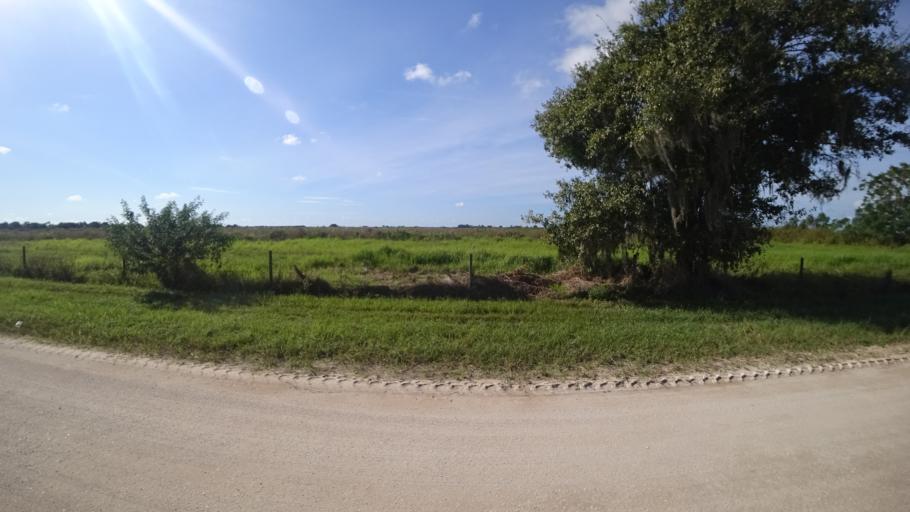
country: US
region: Florida
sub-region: Sarasota County
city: The Meadows
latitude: 27.4676
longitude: -82.3386
